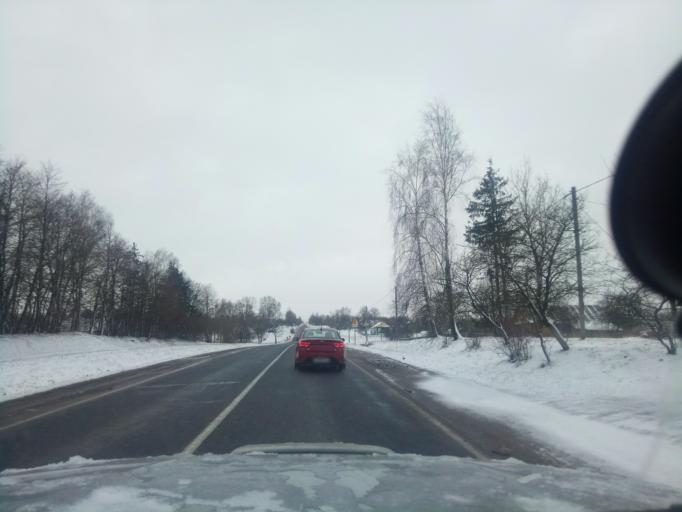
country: BY
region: Minsk
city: Klyetsk
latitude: 53.1330
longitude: 26.6734
